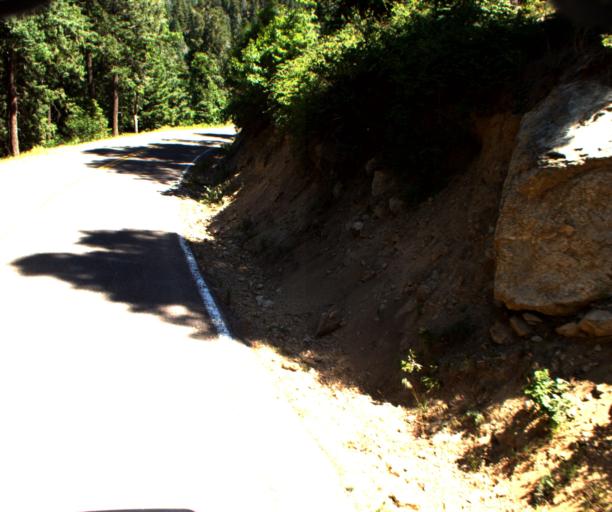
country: US
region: Arizona
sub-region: Graham County
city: Swift Trail Junction
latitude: 32.6284
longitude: -109.8258
